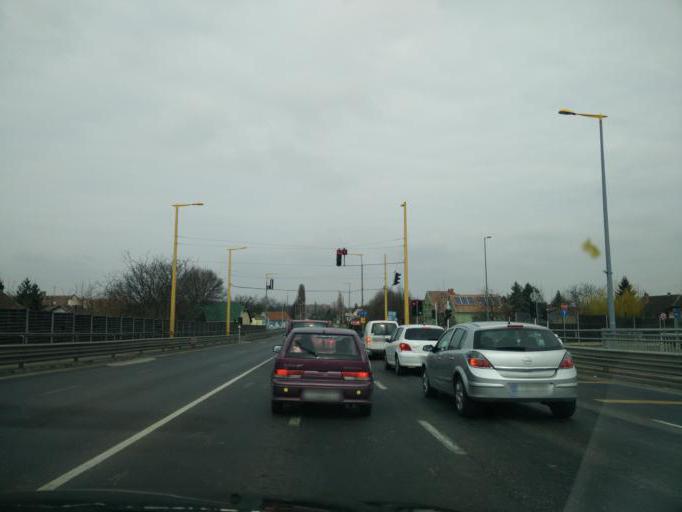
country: HU
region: Gyor-Moson-Sopron
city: Gyor
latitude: 47.6970
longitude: 17.6375
